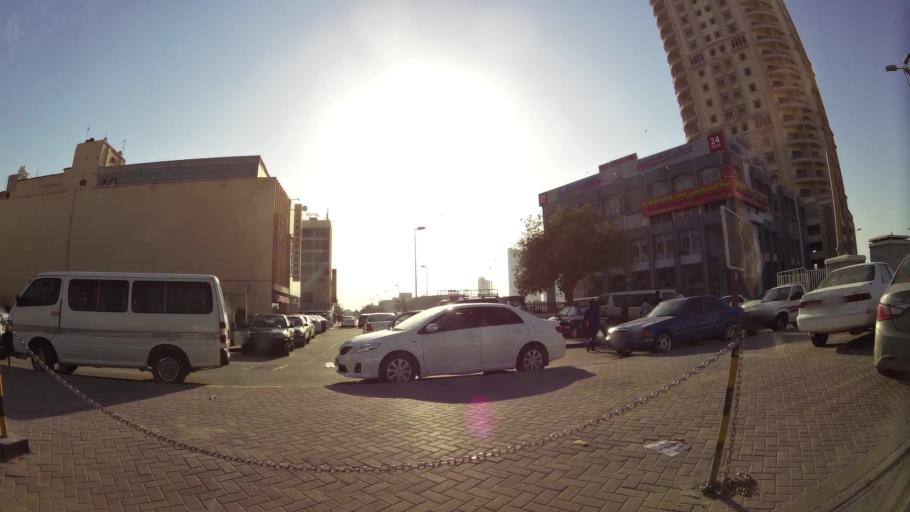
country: BH
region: Manama
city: Manama
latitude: 26.2305
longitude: 50.5710
